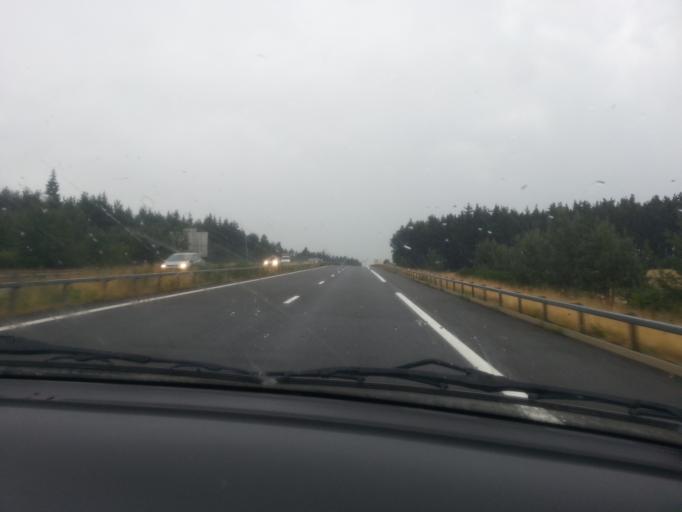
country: FR
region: Languedoc-Roussillon
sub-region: Departement de la Lozere
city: Aumont-Aubrac
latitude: 44.7696
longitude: 3.2841
